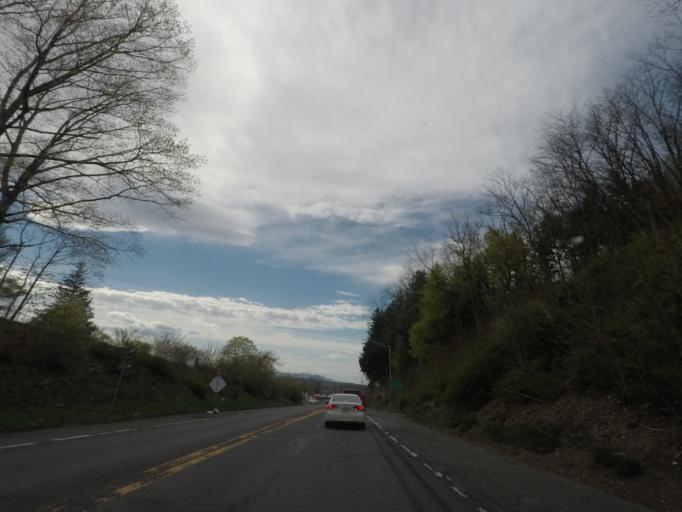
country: US
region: New York
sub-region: Greene County
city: Catskill
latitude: 42.2262
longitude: -73.8601
